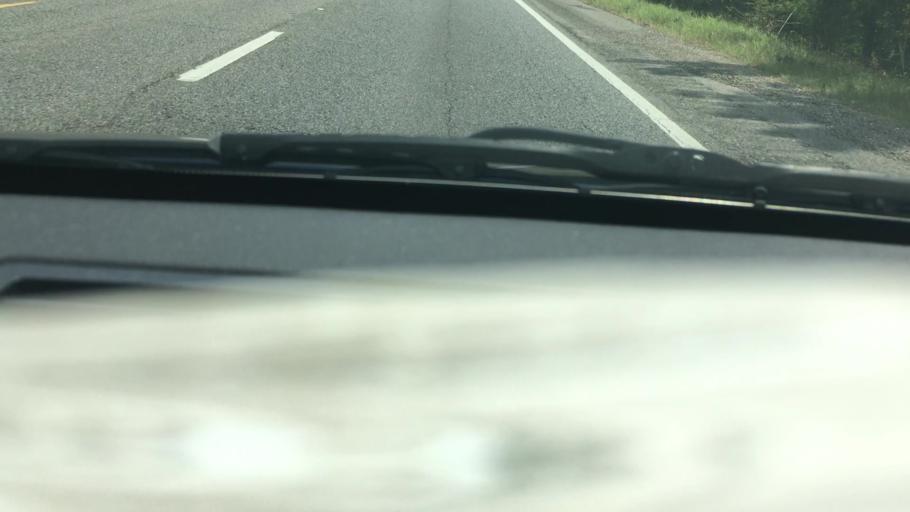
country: US
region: Alabama
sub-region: Tuscaloosa County
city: Northport
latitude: 33.2700
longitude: -87.7395
